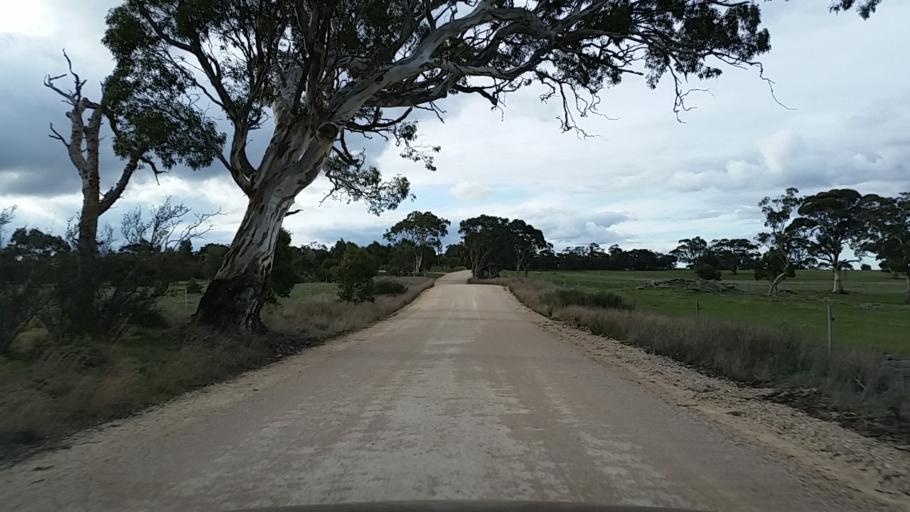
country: AU
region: South Australia
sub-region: Mount Barker
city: Callington
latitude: -34.9896
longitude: 139.0569
